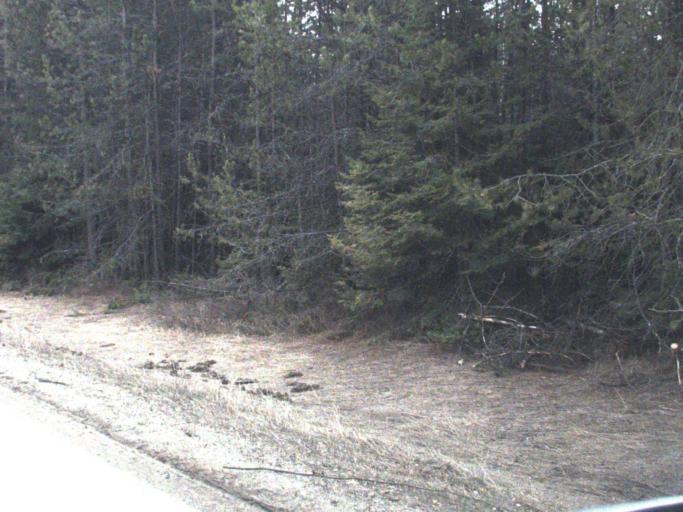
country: US
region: Washington
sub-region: Pend Oreille County
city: Newport
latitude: 48.2724
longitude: -117.2619
